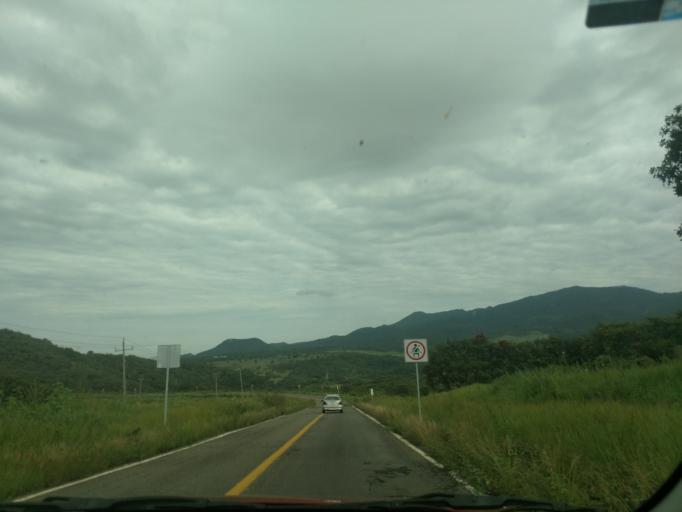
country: MX
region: Jalisco
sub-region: Atengo
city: Soyatlan del Oro
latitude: 20.5484
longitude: -104.2992
